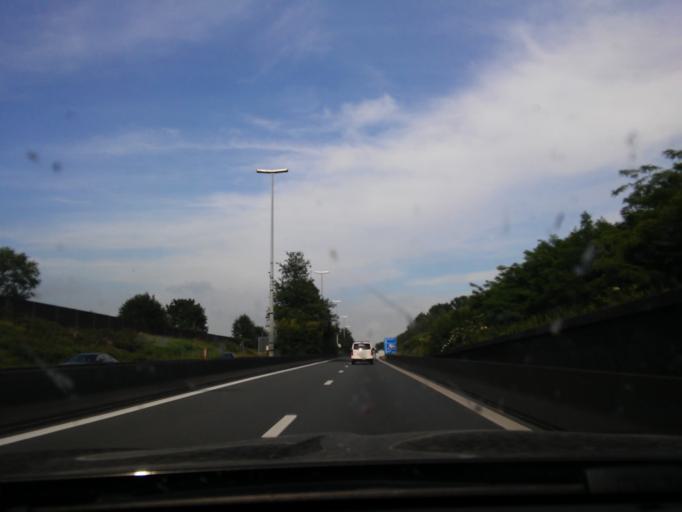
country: BE
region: Flanders
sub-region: Provincie Oost-Vlaanderen
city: Zelzate
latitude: 51.1923
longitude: 3.8079
